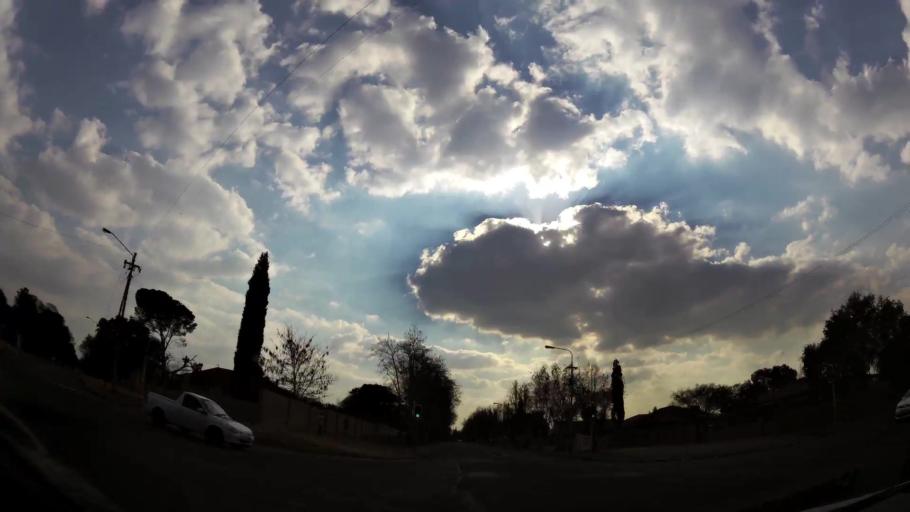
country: ZA
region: Gauteng
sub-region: Ekurhuleni Metropolitan Municipality
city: Germiston
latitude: -26.2298
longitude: 28.1822
